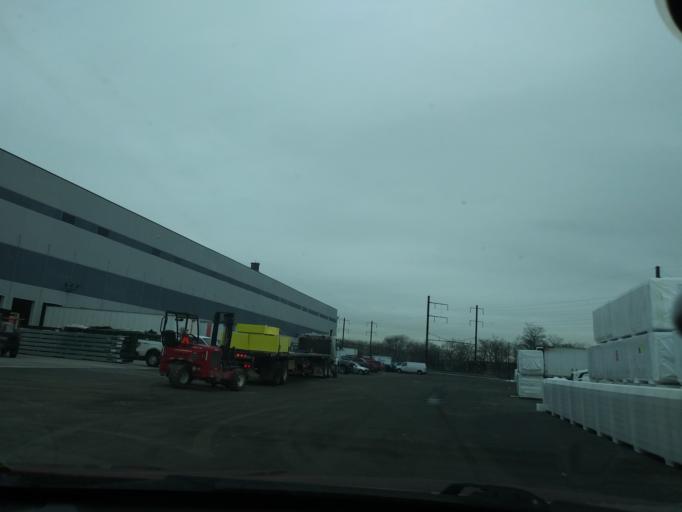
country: US
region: New Jersey
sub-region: Essex County
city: Newark
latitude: 40.7159
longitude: -74.1779
